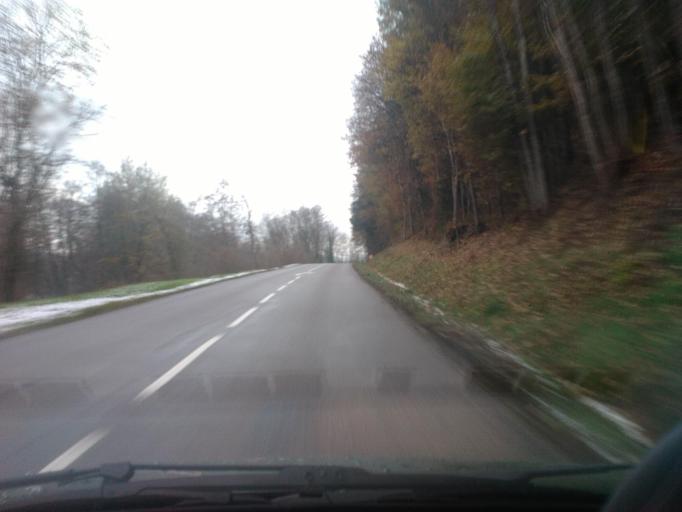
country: FR
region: Lorraine
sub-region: Departement des Vosges
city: Sainte-Marguerite
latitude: 48.2752
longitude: 7.0294
